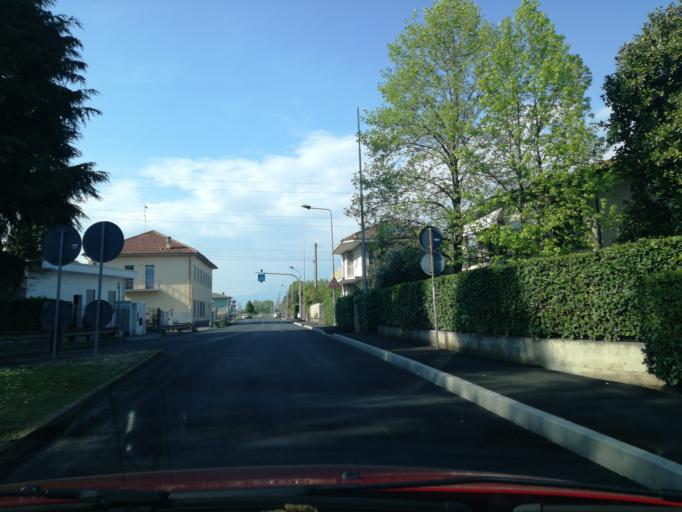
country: IT
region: Lombardy
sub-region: Provincia di Monza e Brianza
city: Cornate d'Adda
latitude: 45.6354
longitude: 9.4718
